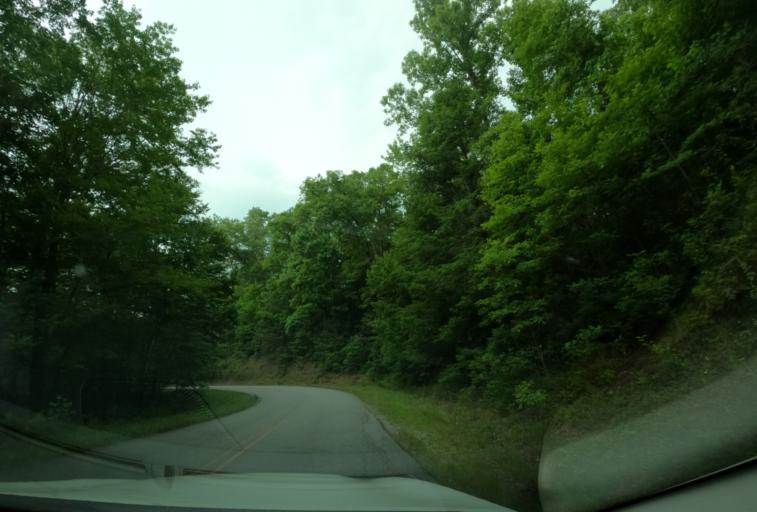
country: US
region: North Carolina
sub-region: Transylvania County
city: Brevard
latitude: 35.2815
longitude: -82.8136
